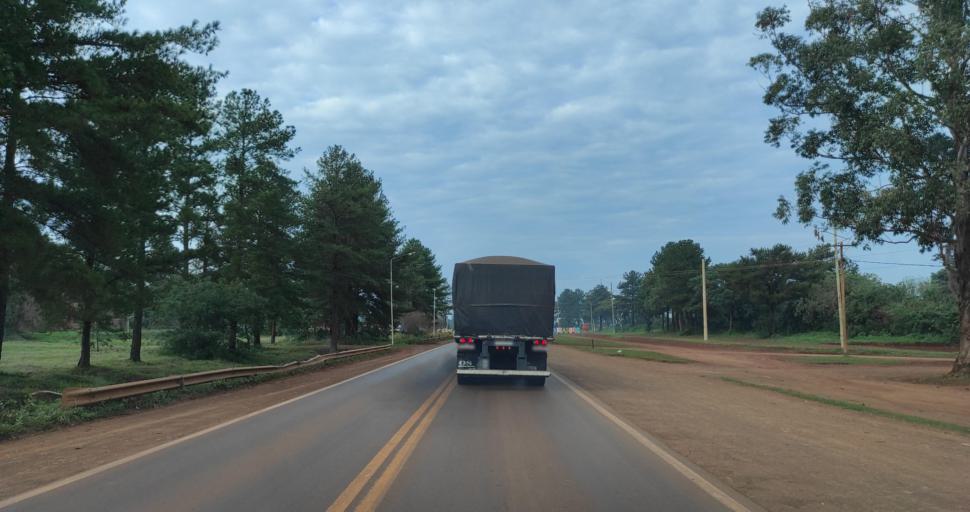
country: AR
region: Corrientes
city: Gobernador Ingeniero Valentin Virasoro
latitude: -28.0267
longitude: -56.0147
